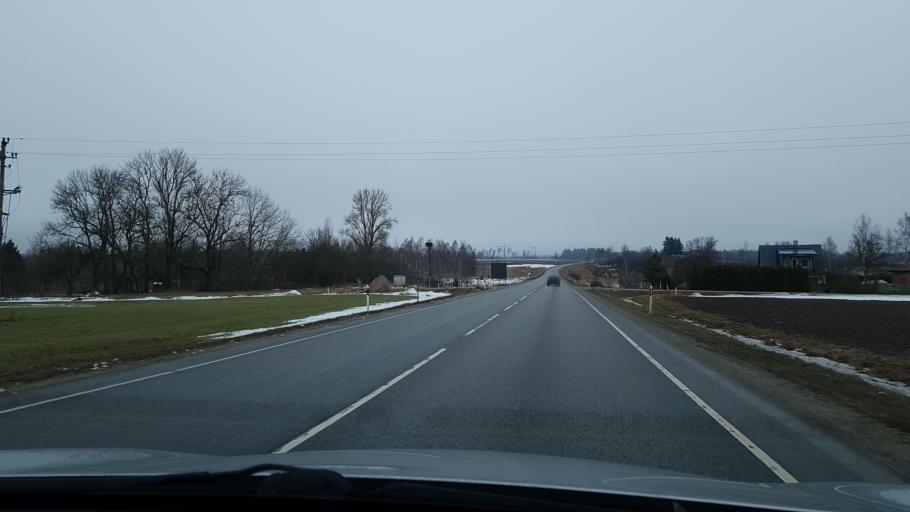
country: EE
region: Tartu
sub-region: Elva linn
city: Elva
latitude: 58.1904
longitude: 26.3506
